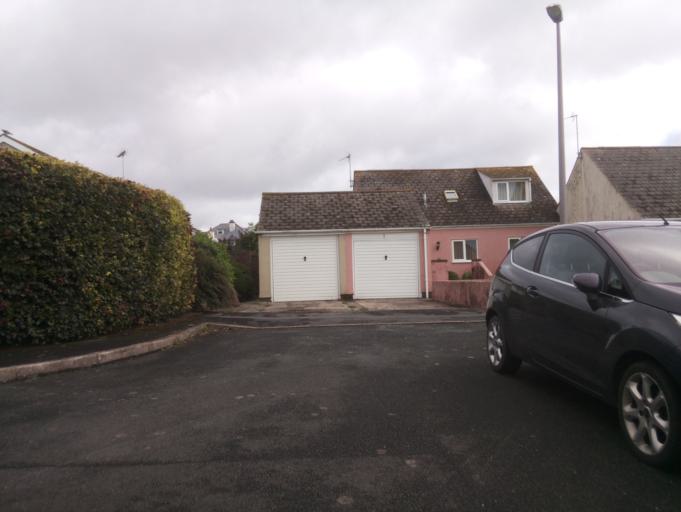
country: GB
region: England
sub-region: Devon
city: Dartmouth
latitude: 50.3299
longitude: -3.5980
